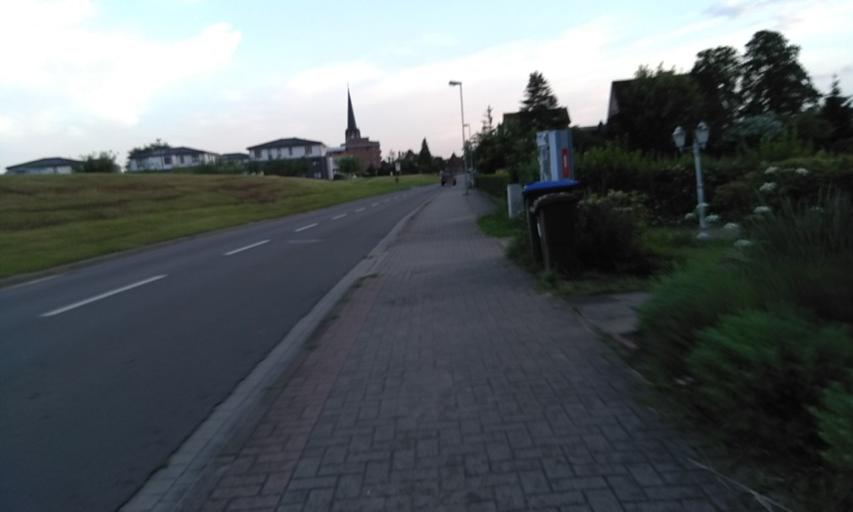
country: DE
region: Lower Saxony
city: Buxtehude
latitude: 53.4817
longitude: 9.7027
